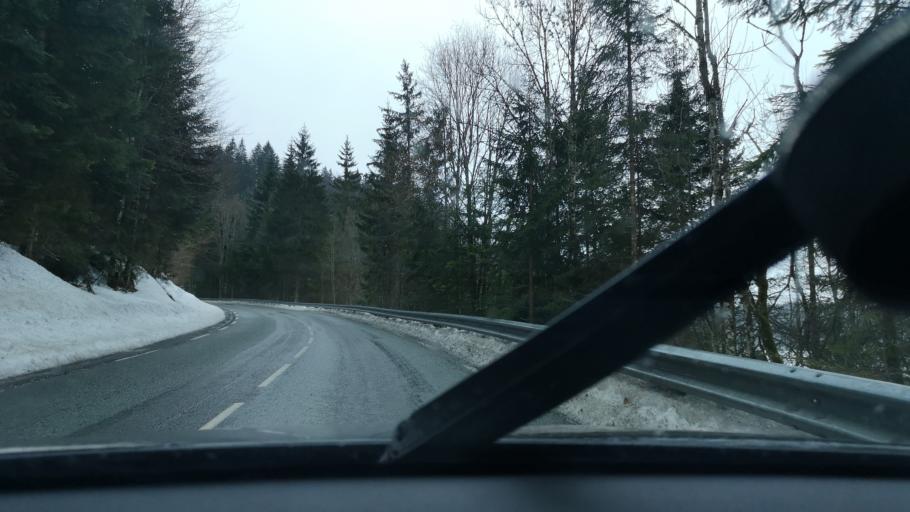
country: FR
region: Franche-Comte
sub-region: Departement du Doubs
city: La Cluse-et-Mijoux
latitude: 46.8596
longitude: 6.3802
